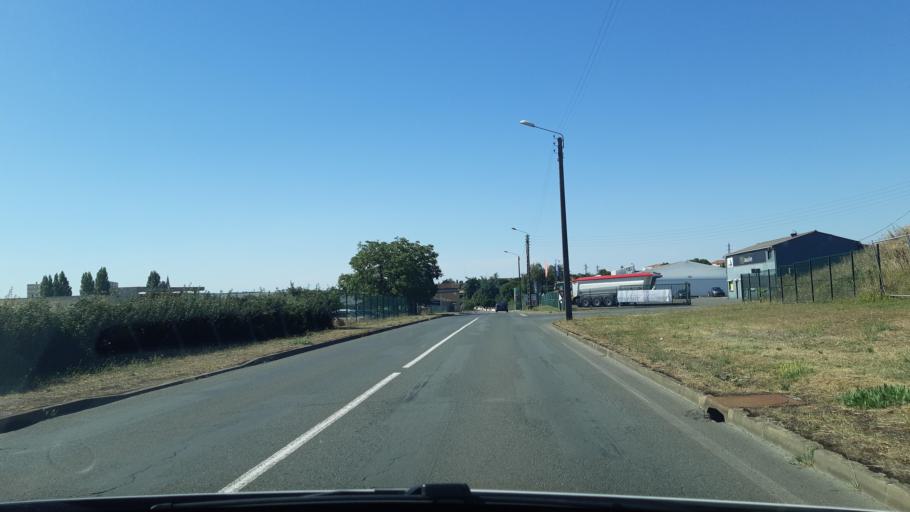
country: FR
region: Poitou-Charentes
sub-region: Departement des Deux-Sevres
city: Exireuil
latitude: 46.4228
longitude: -0.2060
